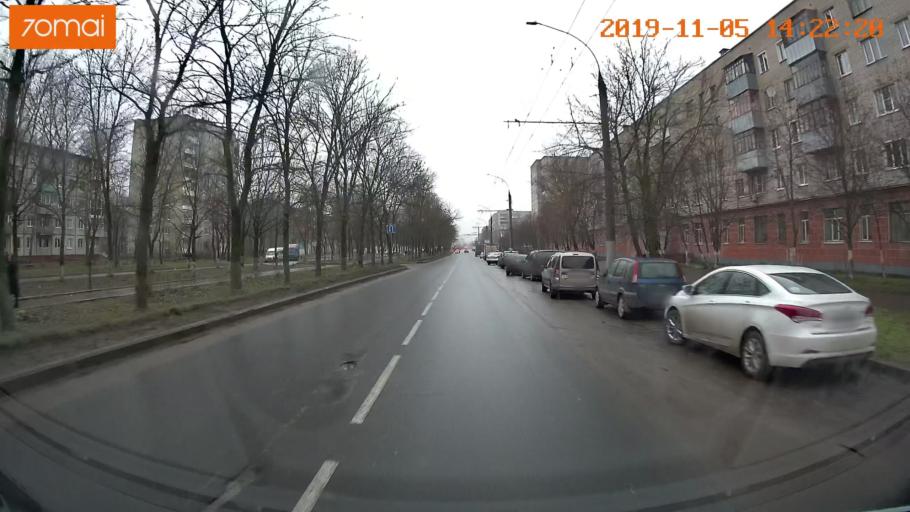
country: RU
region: Ivanovo
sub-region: Gorod Ivanovo
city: Ivanovo
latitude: 56.9629
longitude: 41.0054
